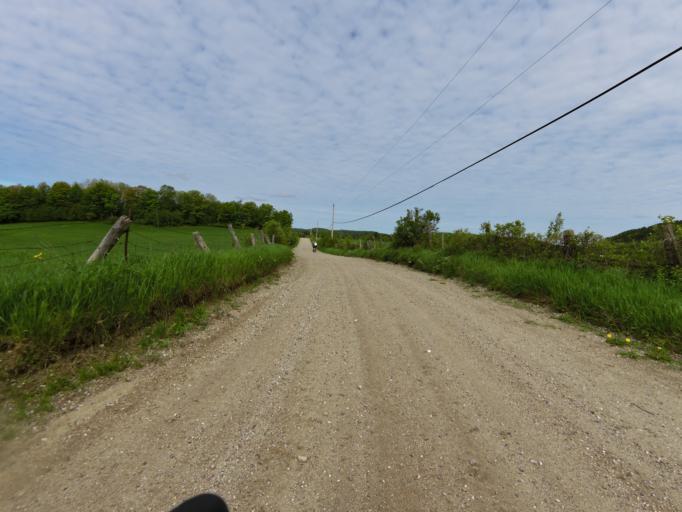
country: CA
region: Quebec
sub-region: Outaouais
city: Wakefield
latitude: 45.7471
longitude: -75.8950
